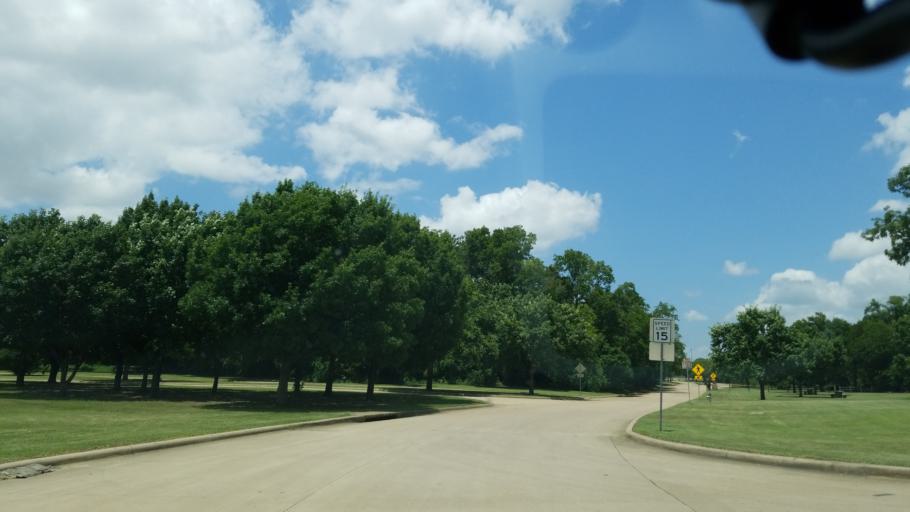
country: US
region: Texas
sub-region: Dallas County
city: Carrollton
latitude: 32.9525
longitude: -96.9369
